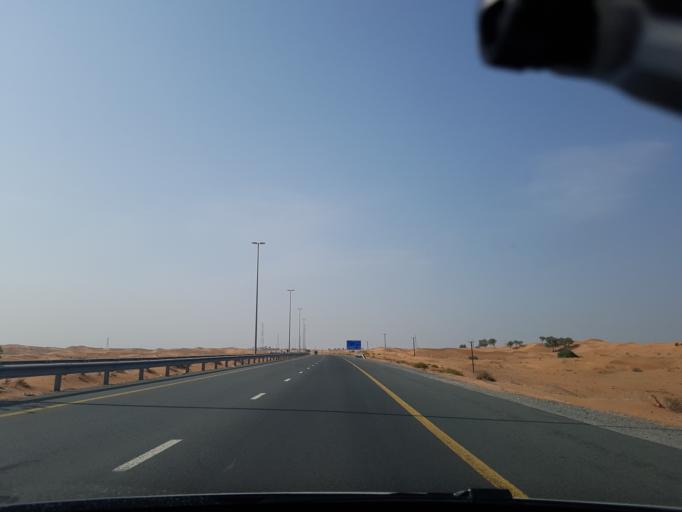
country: AE
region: Umm al Qaywayn
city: Umm al Qaywayn
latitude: 25.5204
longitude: 55.7397
